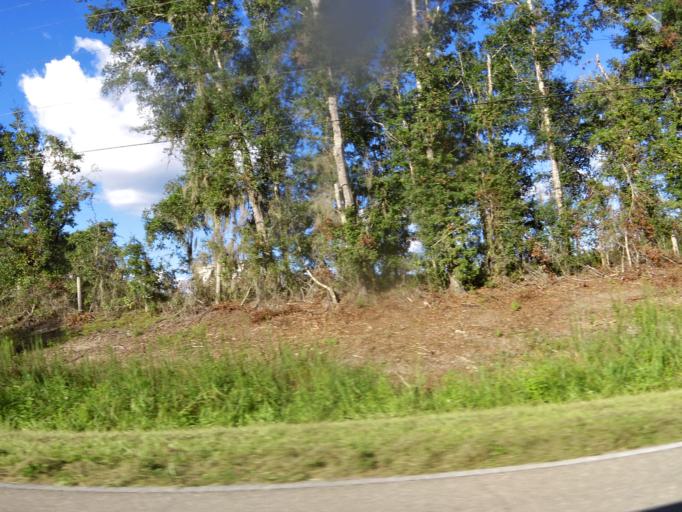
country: US
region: Florida
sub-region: Wakulla County
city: Crawfordville
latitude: 30.0698
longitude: -84.5070
